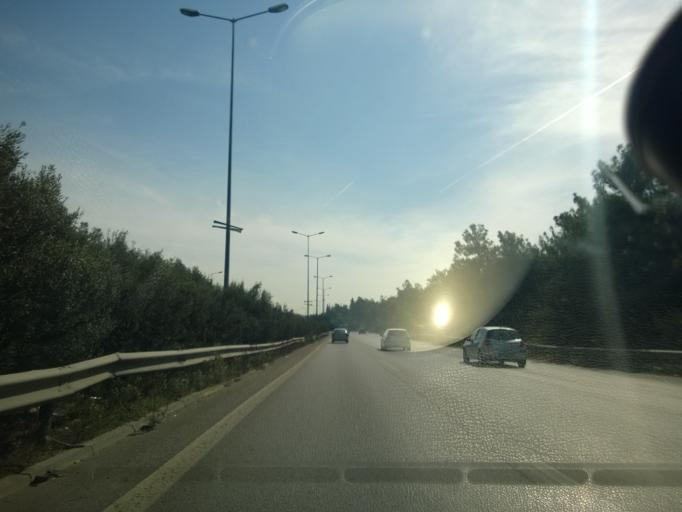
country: GR
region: Central Macedonia
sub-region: Nomos Thessalonikis
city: Triandria
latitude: 40.6194
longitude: 22.9830
